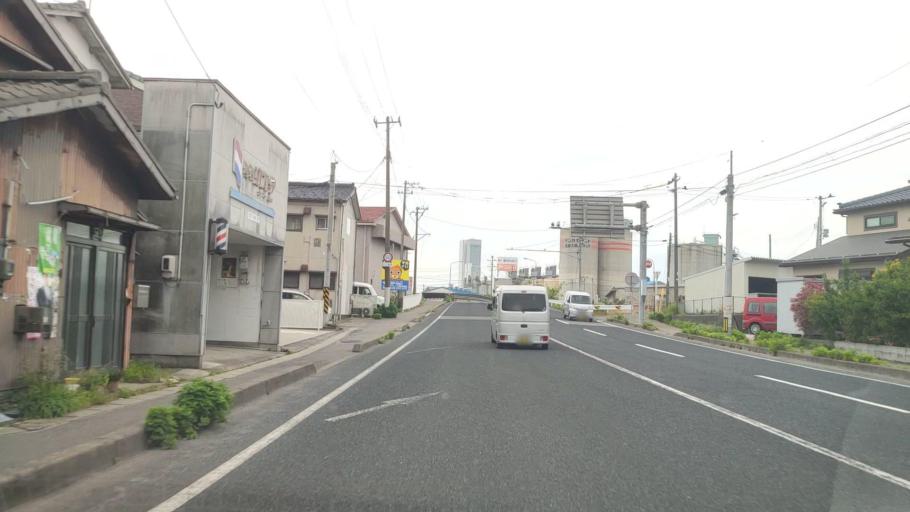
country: JP
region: Niigata
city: Niigata-shi
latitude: 37.9325
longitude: 139.0717
